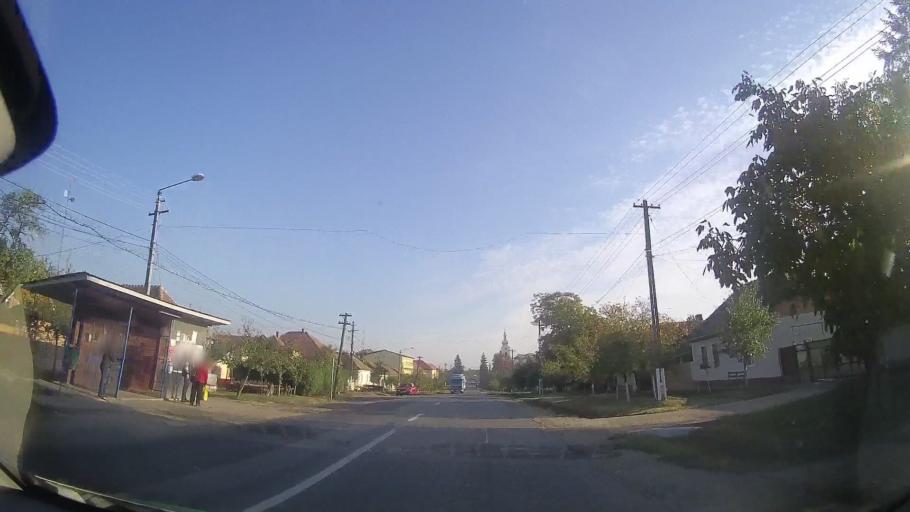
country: RO
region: Timis
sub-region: Comuna Fibis
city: Fibis
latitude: 45.9719
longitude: 21.4211
